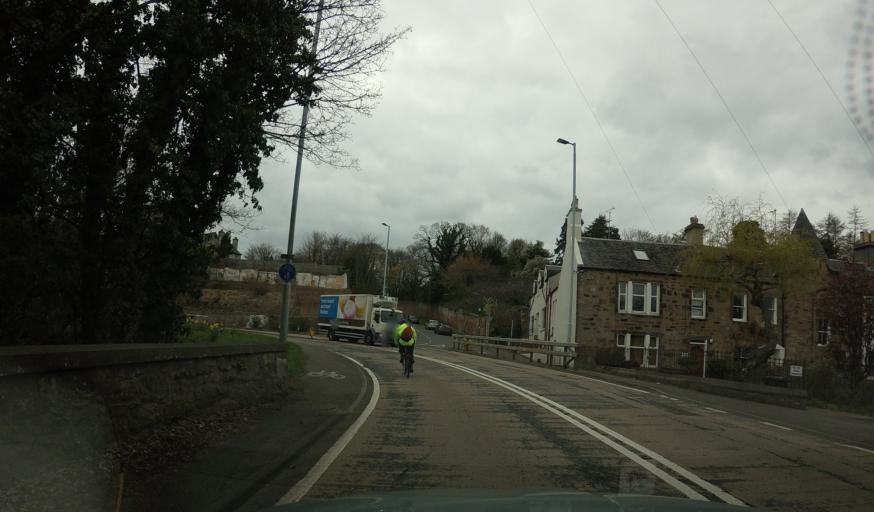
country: GB
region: Scotland
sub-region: Midlothian
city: Dalkeith
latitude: 55.8967
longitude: -3.0738
